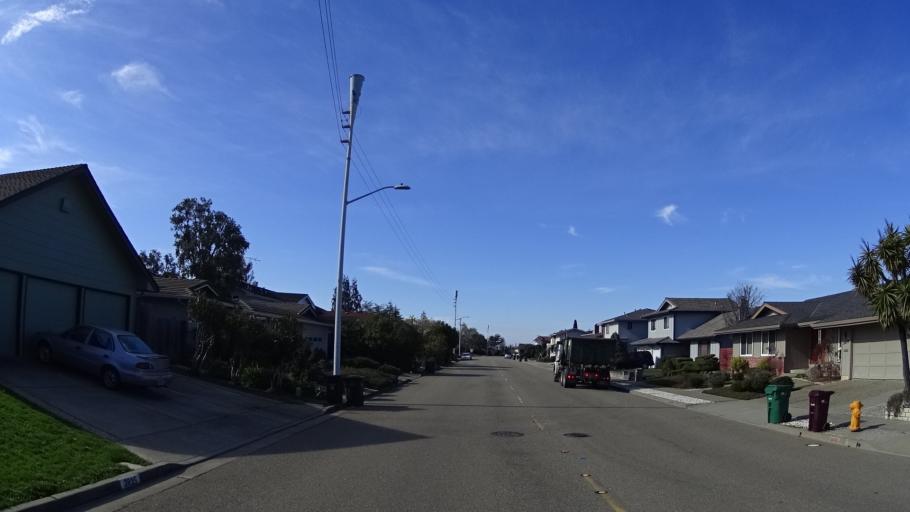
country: US
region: California
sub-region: Alameda County
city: Fairview
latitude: 37.6616
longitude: -122.0328
